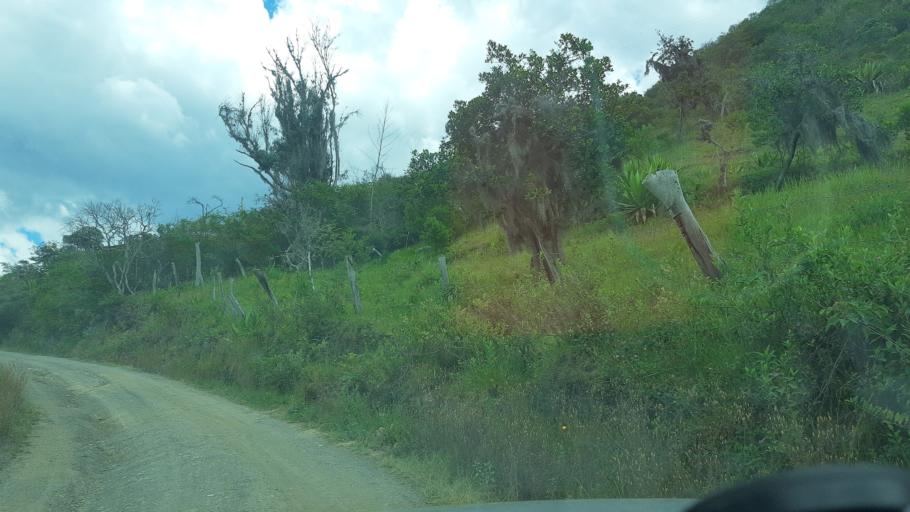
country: CO
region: Boyaca
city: Santa Sofia
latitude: 5.7051
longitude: -73.5636
